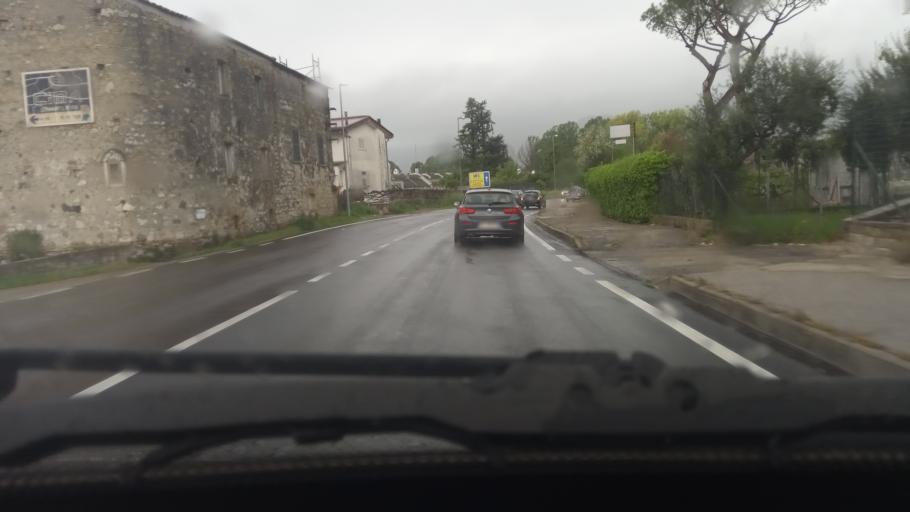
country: IT
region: Latium
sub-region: Provincia di Latina
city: Penitro
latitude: 41.2627
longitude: 13.6818
